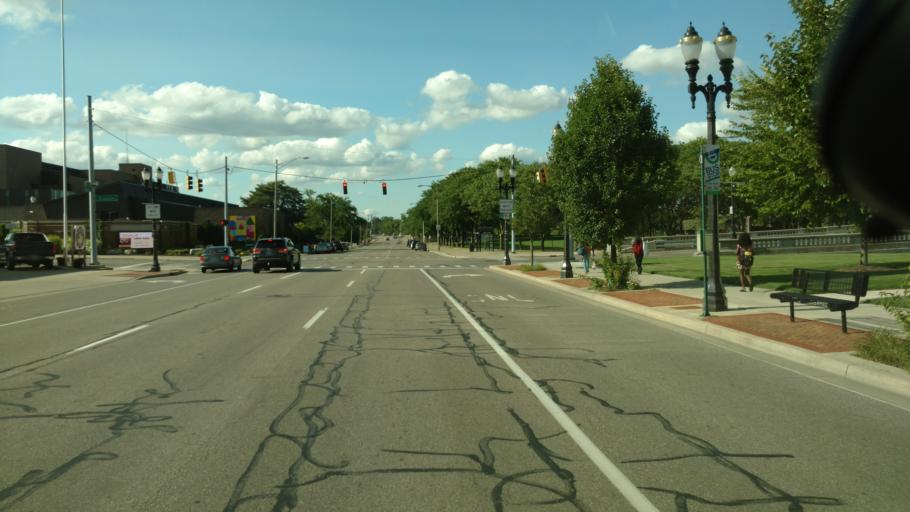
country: US
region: Michigan
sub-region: Ingham County
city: Lansing
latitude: 42.7368
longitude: -84.5506
